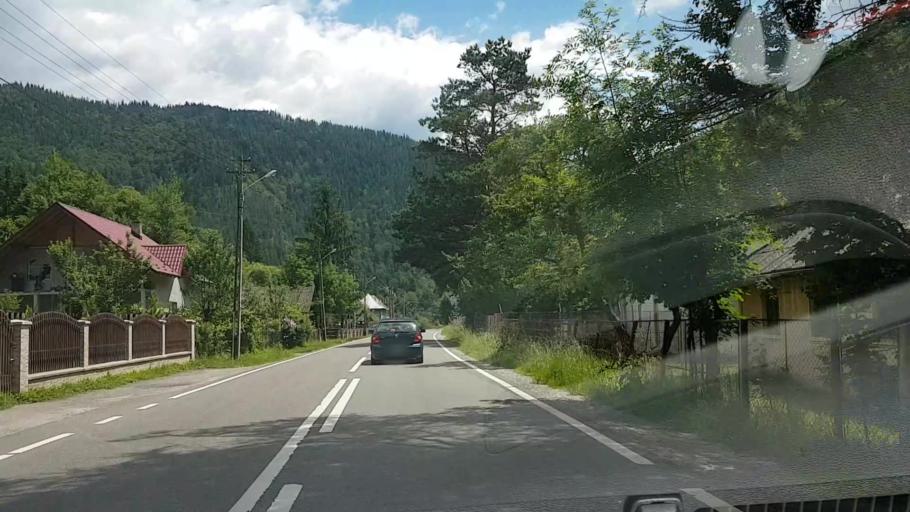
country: RO
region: Suceava
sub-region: Comuna Crucea
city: Crucea
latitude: 47.2834
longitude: 25.6379
